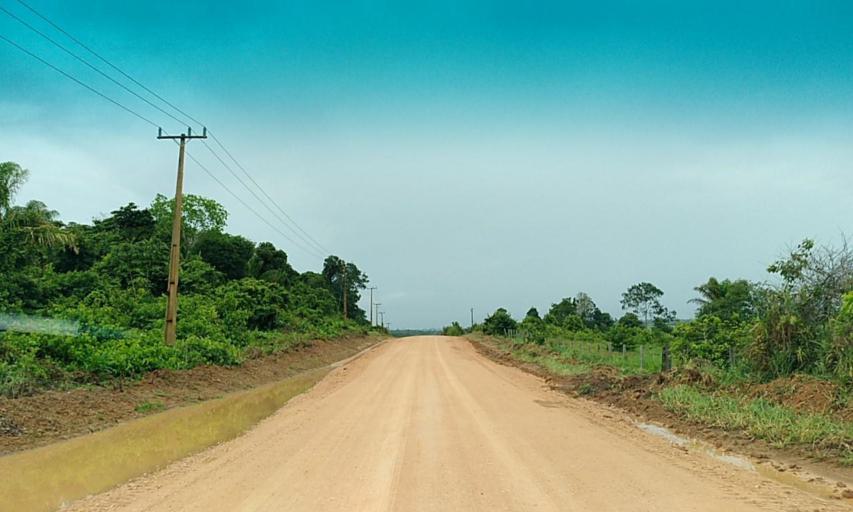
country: BR
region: Para
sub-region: Senador Jose Porfirio
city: Senador Jose Porfirio
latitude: -3.0593
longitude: -51.6520
